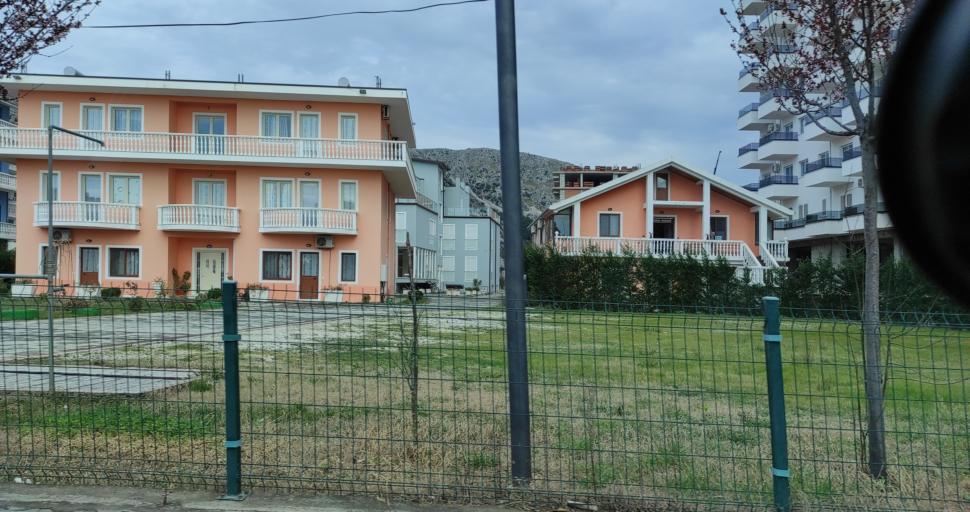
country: AL
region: Lezhe
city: Shengjin
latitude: 41.8041
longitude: 19.6003
